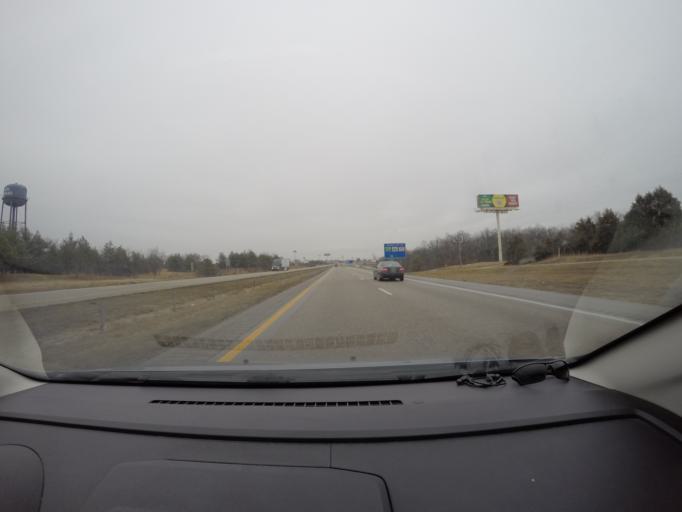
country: US
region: Missouri
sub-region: Montgomery County
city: Montgomery City
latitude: 38.9021
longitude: -91.4699
